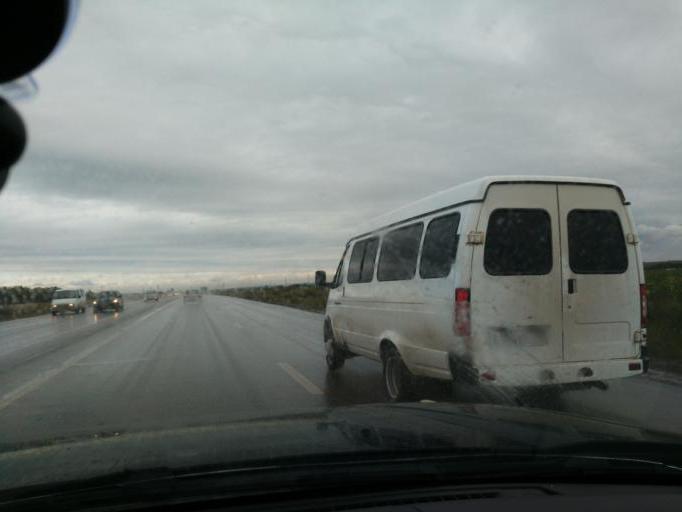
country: RU
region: Perm
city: Kultayevo
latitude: 57.8799
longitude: 55.9129
